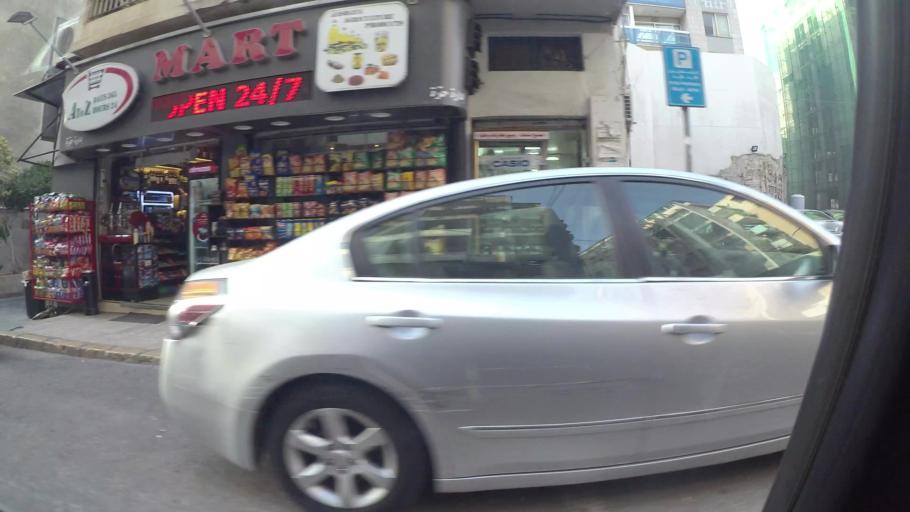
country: LB
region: Beyrouth
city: Ra's Bayrut
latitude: 33.8981
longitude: 35.4794
